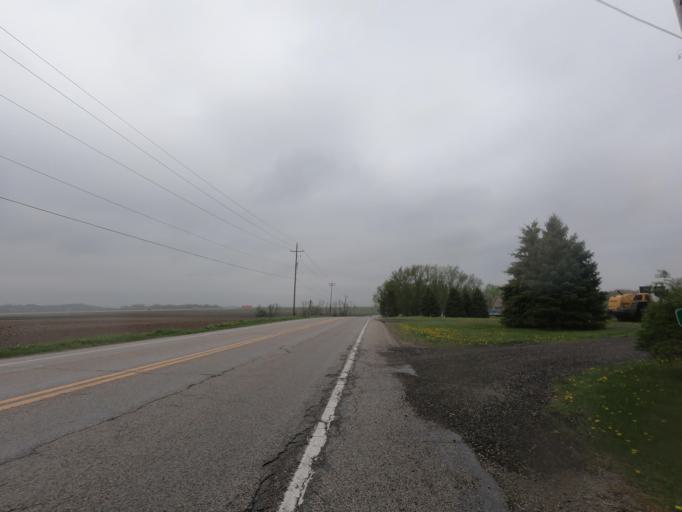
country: US
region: Wisconsin
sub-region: Jefferson County
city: Jefferson
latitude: 43.0241
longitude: -88.8186
